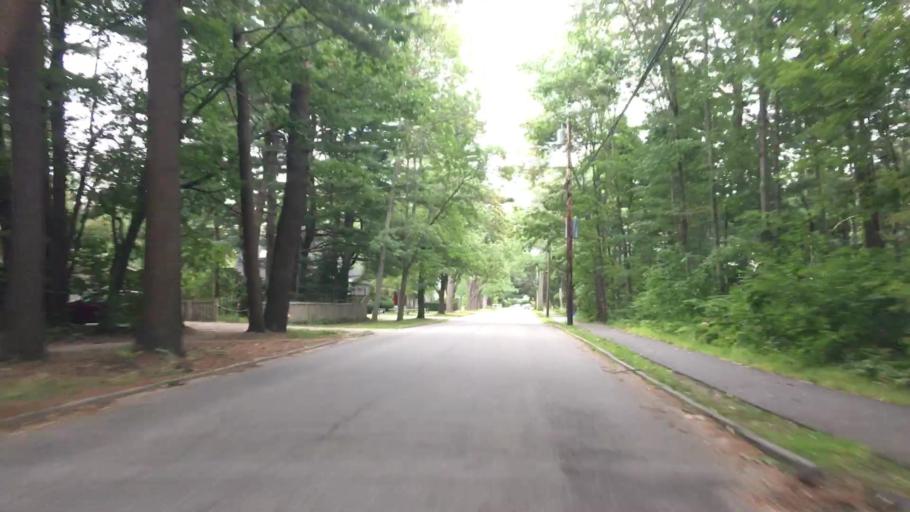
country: US
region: Maine
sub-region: Cumberland County
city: Brunswick
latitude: 43.9073
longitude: -69.9701
